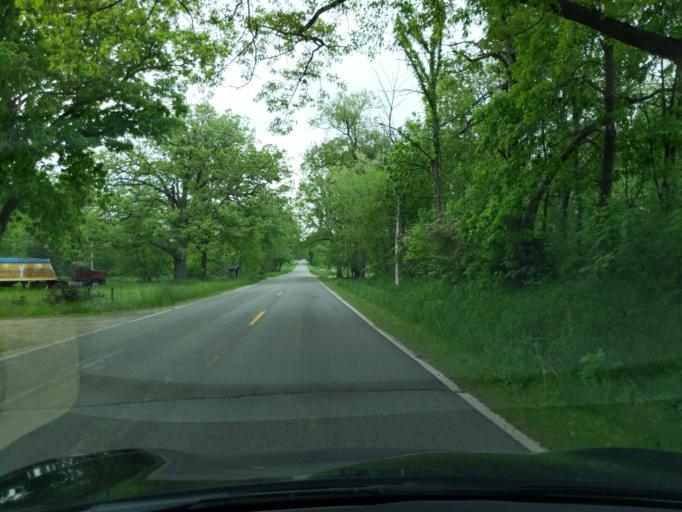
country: US
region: Michigan
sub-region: Ingham County
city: Leslie
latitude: 42.3669
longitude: -84.3490
